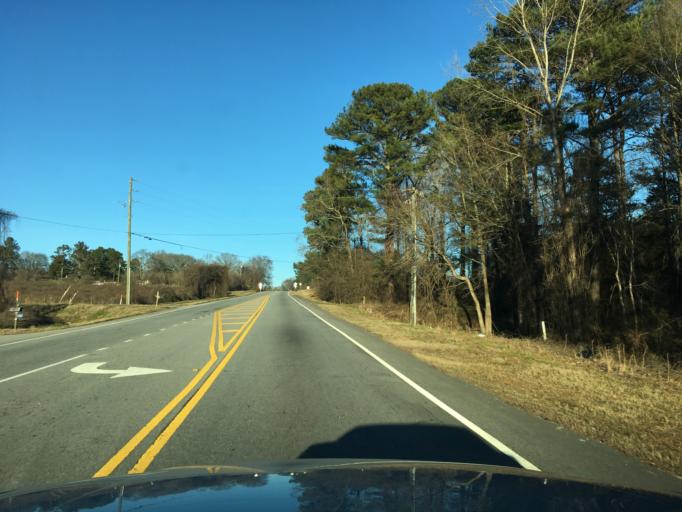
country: US
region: Georgia
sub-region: Barrow County
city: Winder
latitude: 33.9174
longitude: -83.7796
